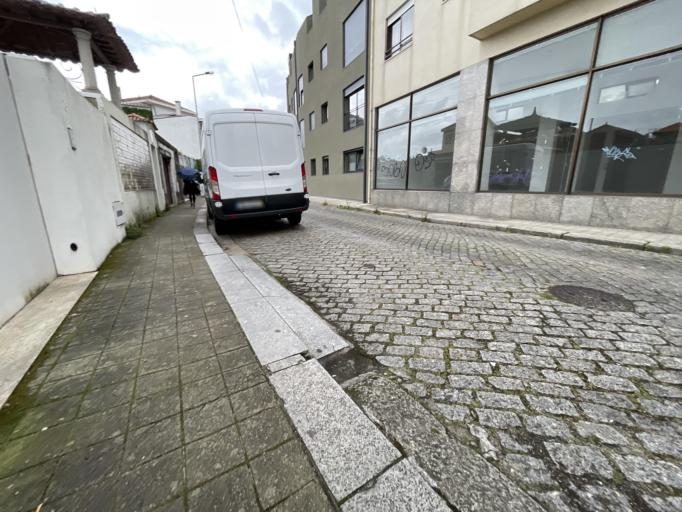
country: PT
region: Porto
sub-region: Porto
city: Porto
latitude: 41.1701
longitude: -8.6091
